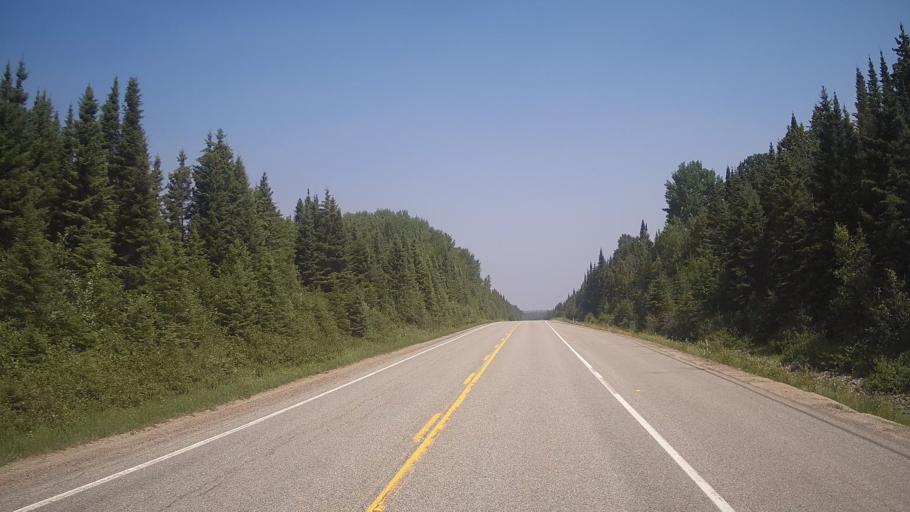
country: CA
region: Ontario
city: Timmins
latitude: 48.2013
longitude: -81.5791
